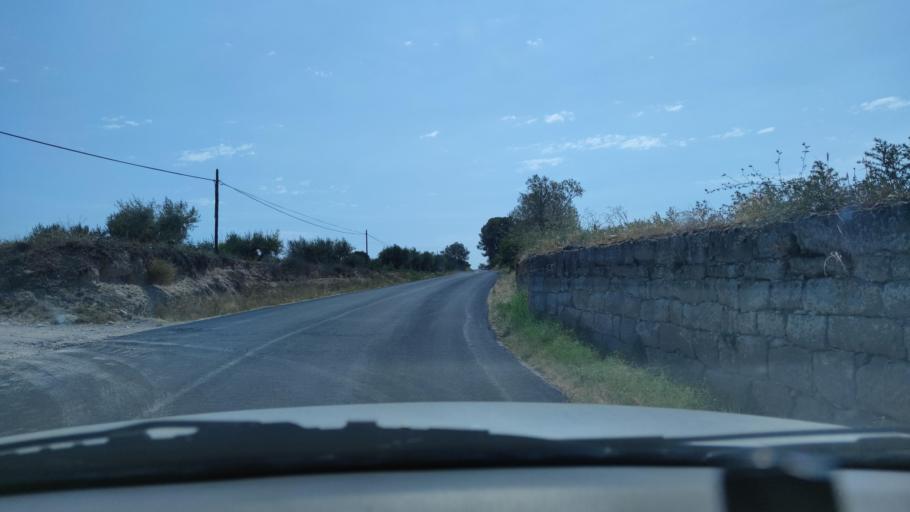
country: ES
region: Catalonia
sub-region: Provincia de Lleida
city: Ivorra
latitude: 41.7820
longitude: 1.3020
